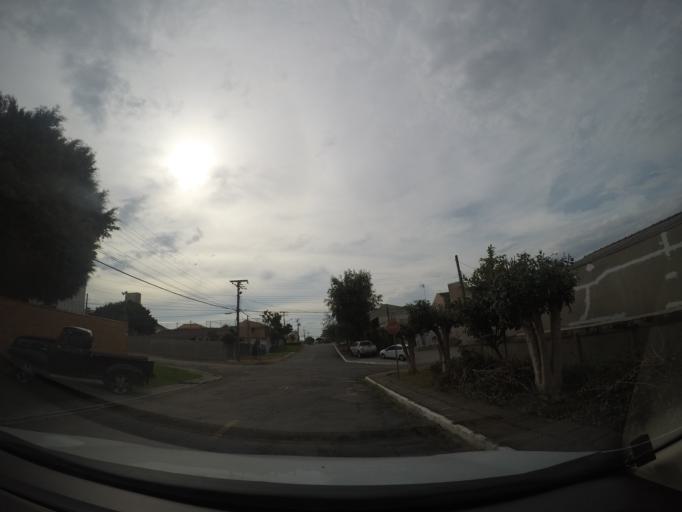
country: BR
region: Parana
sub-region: Sao Jose Dos Pinhais
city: Sao Jose dos Pinhais
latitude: -25.5061
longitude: -49.2624
